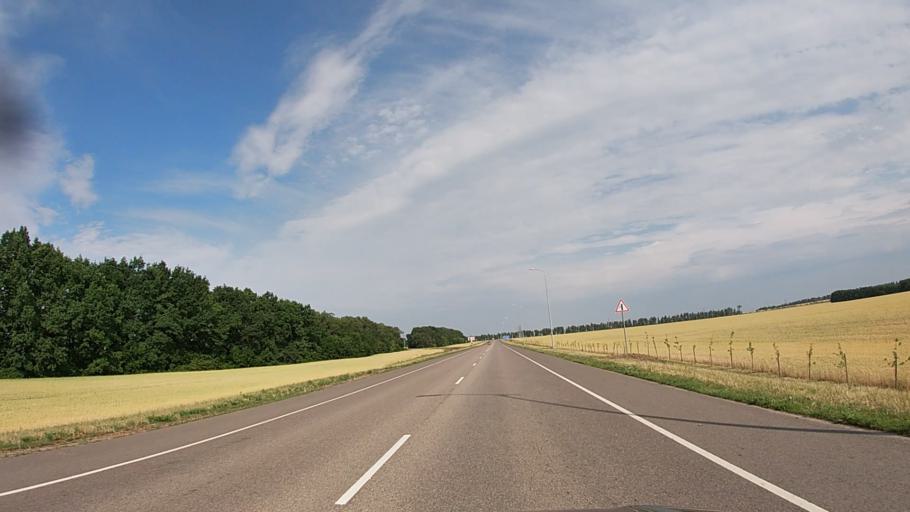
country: RU
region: Belgorod
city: Proletarskiy
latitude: 50.8273
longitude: 35.7770
